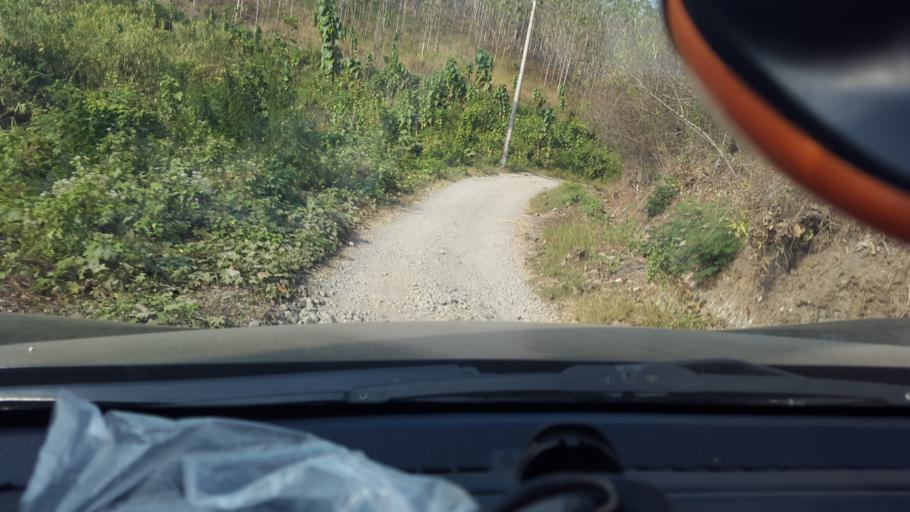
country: ID
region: West Java
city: Cikupa
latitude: -7.3593
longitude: 106.7031
